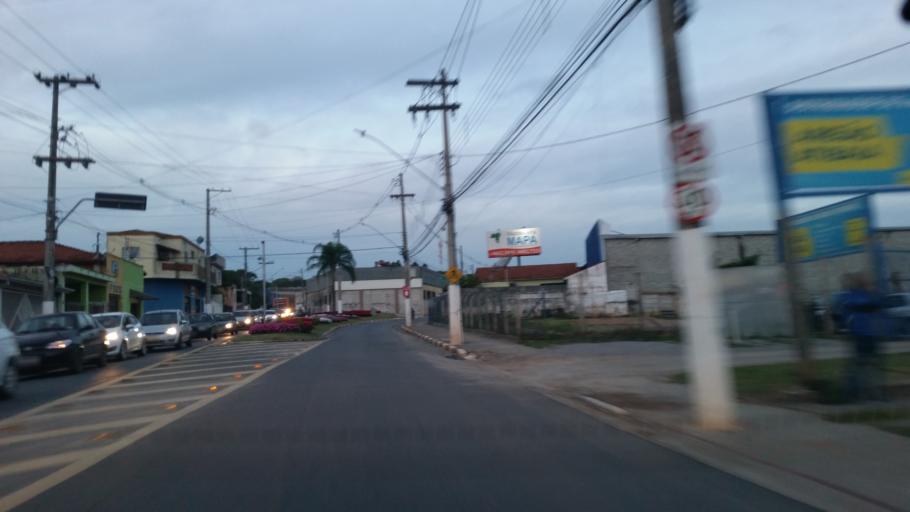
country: BR
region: Sao Paulo
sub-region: Atibaia
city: Atibaia
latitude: -23.1021
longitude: -46.5542
